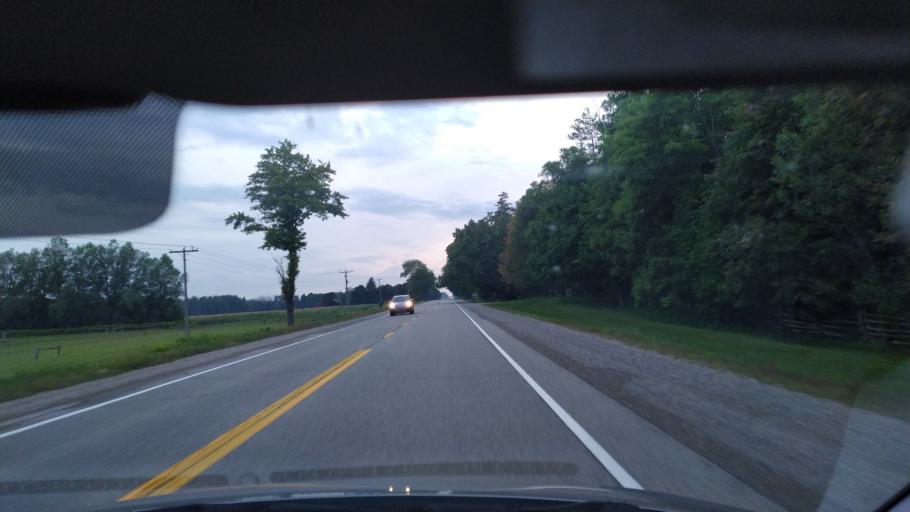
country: CA
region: Ontario
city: Kitchener
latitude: 43.3160
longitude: -80.5407
